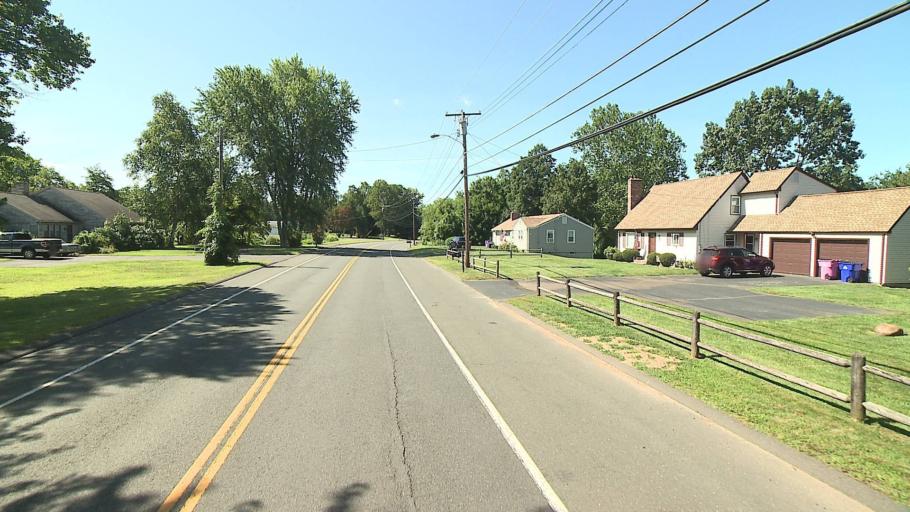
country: US
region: Connecticut
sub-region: Hartford County
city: Tariffville
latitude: 41.9193
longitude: -72.7378
